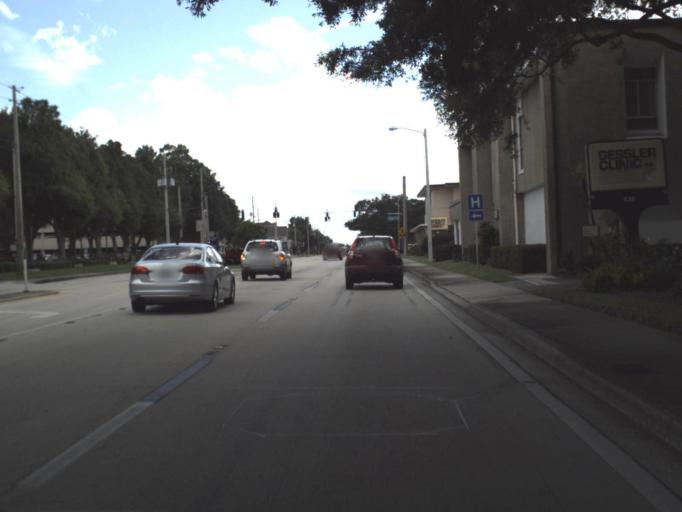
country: US
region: Florida
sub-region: Polk County
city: Winter Haven
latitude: 28.0289
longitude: -81.7269
